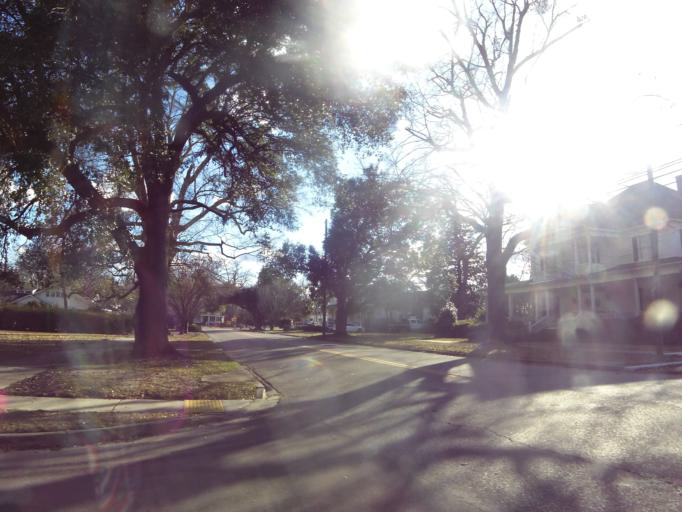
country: US
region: South Carolina
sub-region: Clarendon County
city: Manning
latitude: 33.6926
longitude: -80.2108
